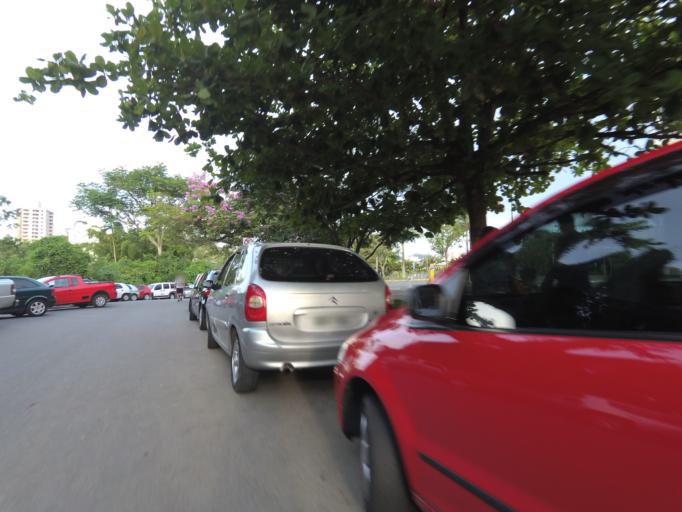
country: BR
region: Santa Catarina
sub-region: Blumenau
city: Blumenau
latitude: -26.9129
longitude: -49.0894
